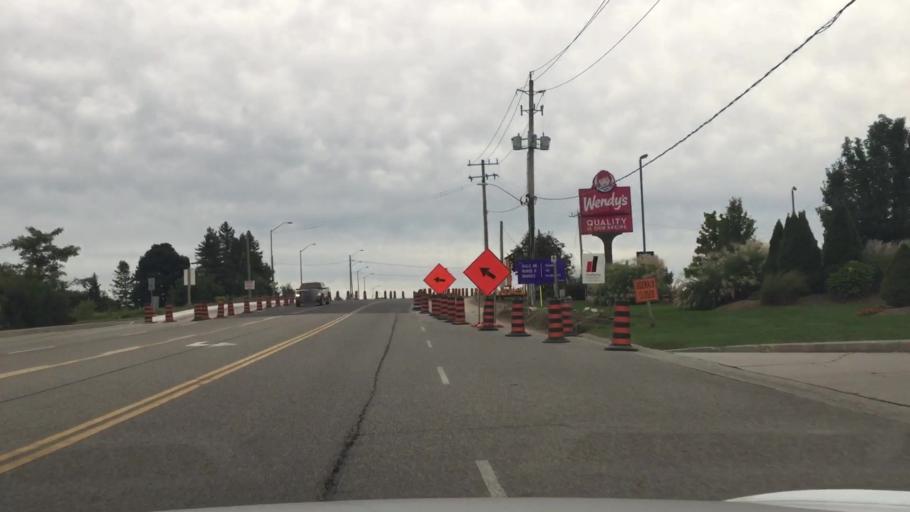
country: CA
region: Ontario
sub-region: Oxford County
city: Woodstock
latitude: 43.1129
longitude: -80.7369
